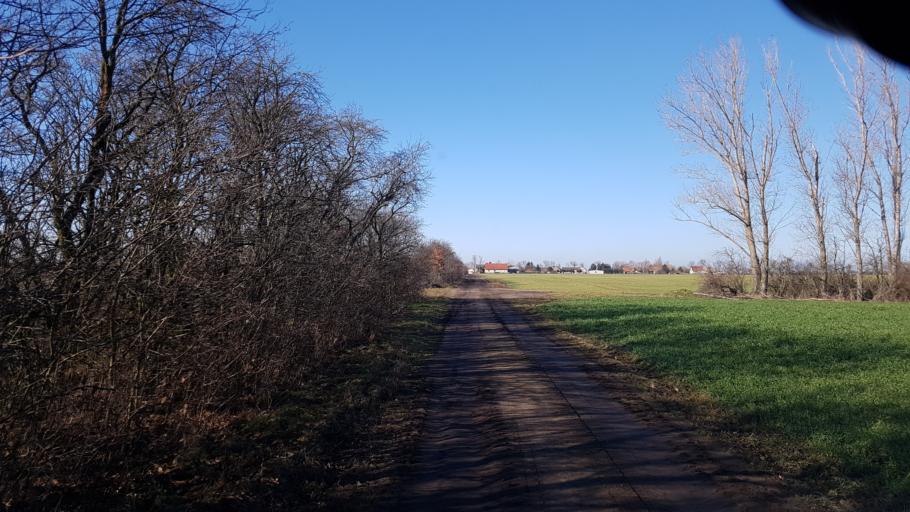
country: DE
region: Brandenburg
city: Muhlberg
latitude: 51.5075
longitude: 13.2364
